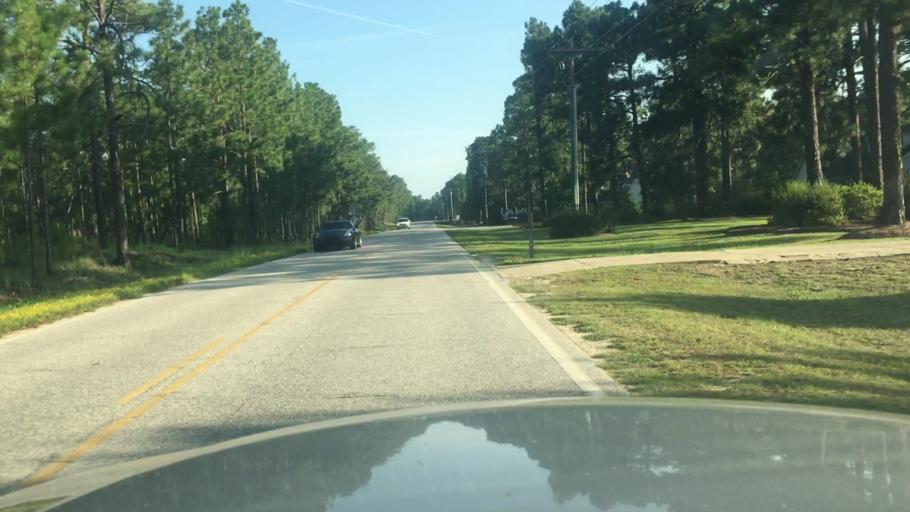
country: US
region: North Carolina
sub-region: Harnett County
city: Walkertown
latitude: 35.2179
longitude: -78.8653
